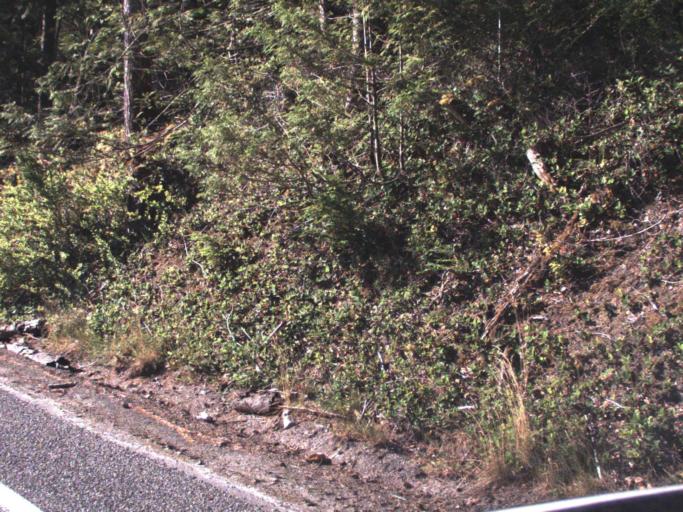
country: US
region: Washington
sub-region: King County
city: Enumclaw
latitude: 47.1600
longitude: -121.8688
